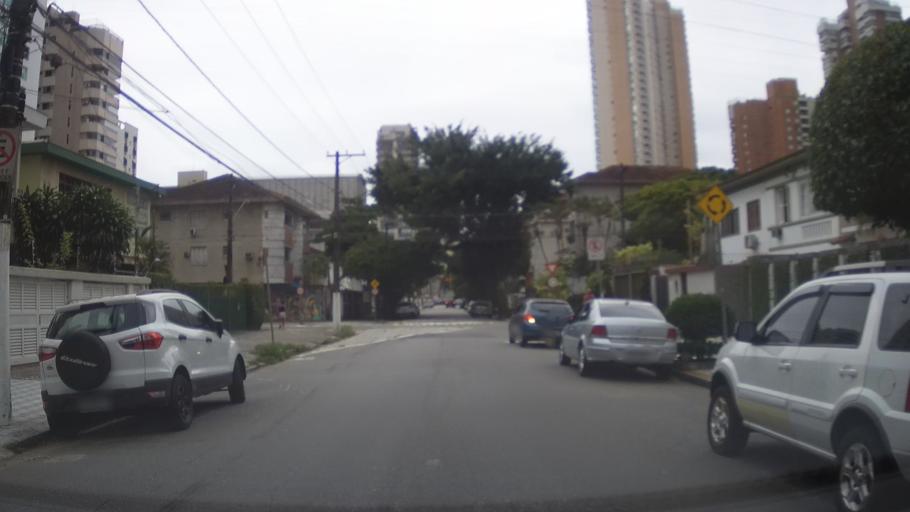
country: BR
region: Sao Paulo
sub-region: Santos
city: Santos
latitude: -23.9711
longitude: -46.3171
